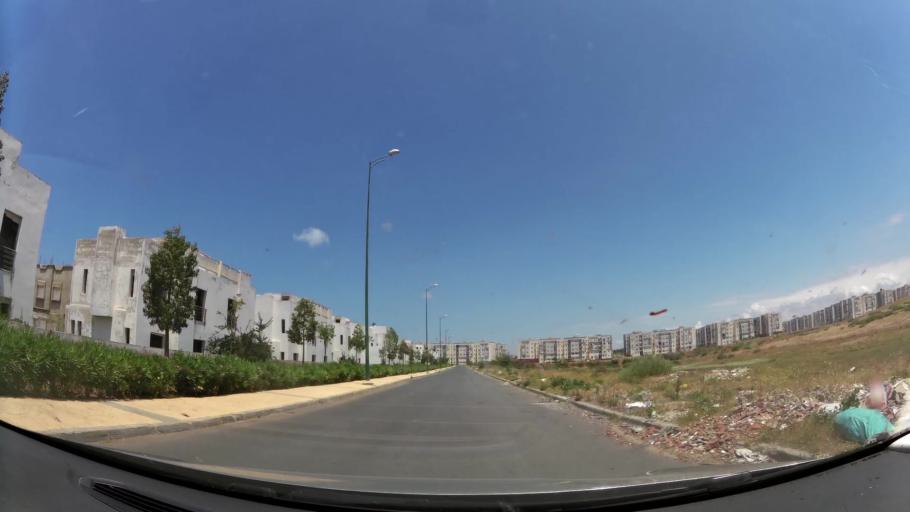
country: MA
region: Gharb-Chrarda-Beni Hssen
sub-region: Kenitra Province
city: Kenitra
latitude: 34.2512
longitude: -6.6482
